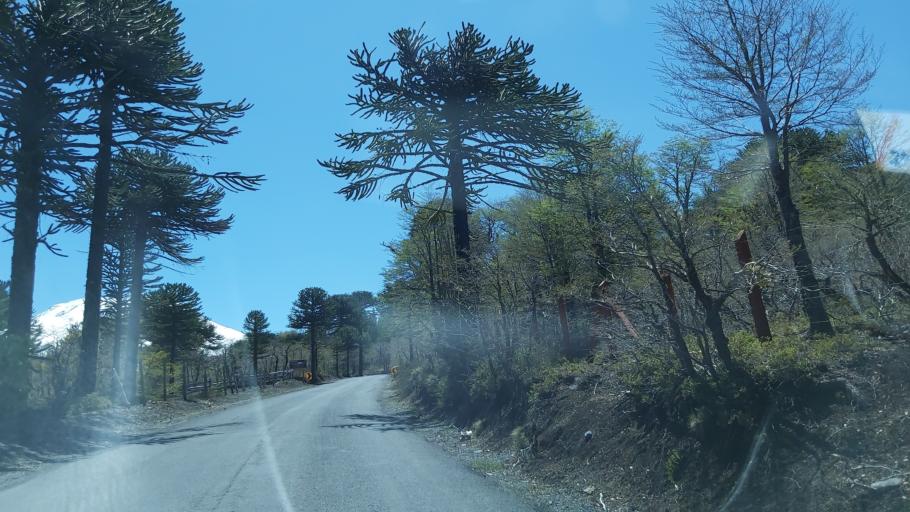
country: CL
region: Araucania
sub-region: Provincia de Cautin
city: Vilcun
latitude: -38.4328
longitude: -71.5364
